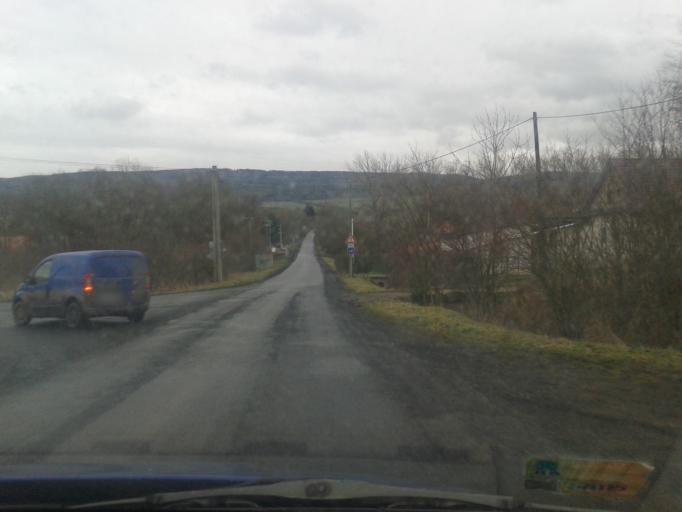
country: CZ
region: Central Bohemia
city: Revnice
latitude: 49.8887
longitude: 14.1485
